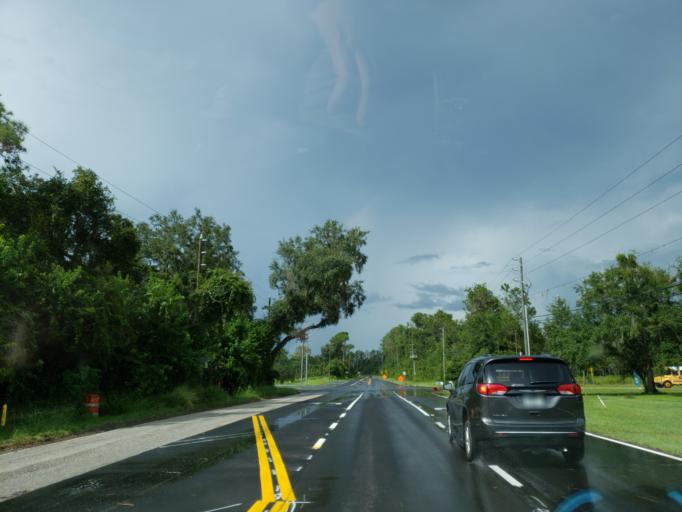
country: US
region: Florida
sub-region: Pasco County
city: Land O' Lakes
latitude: 28.2510
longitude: -82.4498
